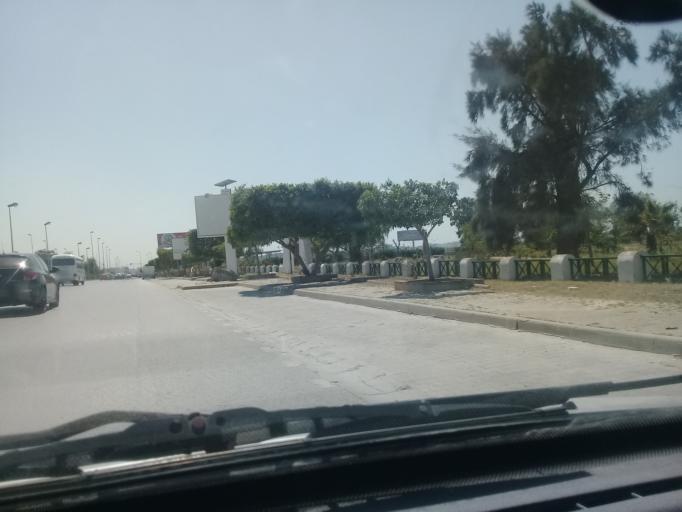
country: TN
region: Ariana
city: Ariana
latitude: 36.8327
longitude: 10.2201
